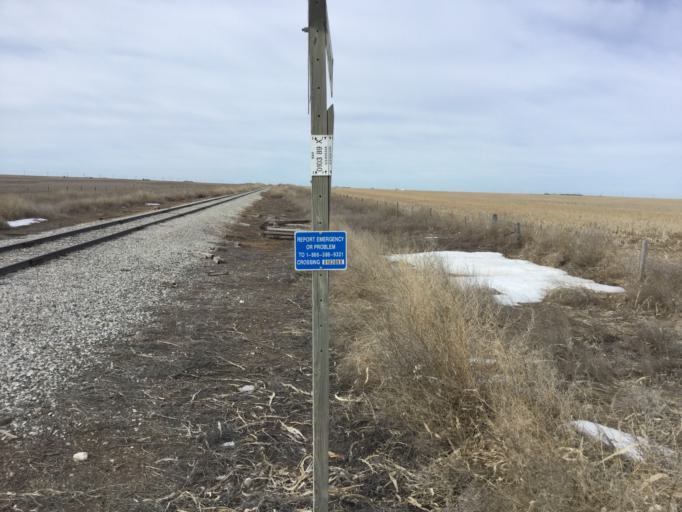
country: US
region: Kansas
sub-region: Lane County
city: Dighton
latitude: 38.4855
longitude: -100.5039
